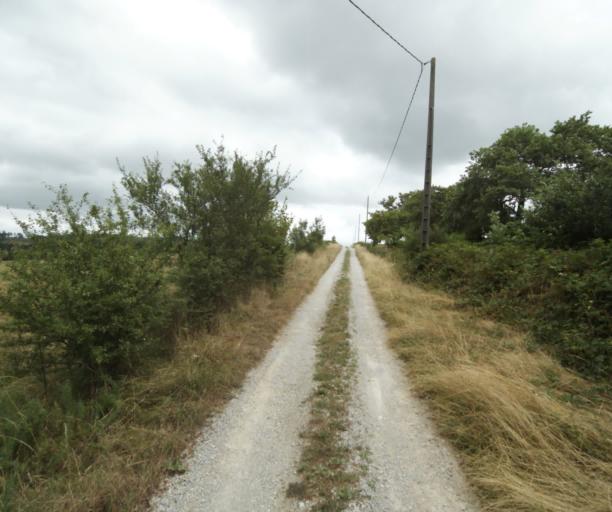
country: FR
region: Midi-Pyrenees
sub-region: Departement du Tarn
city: Soreze
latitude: 43.4324
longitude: 2.1041
